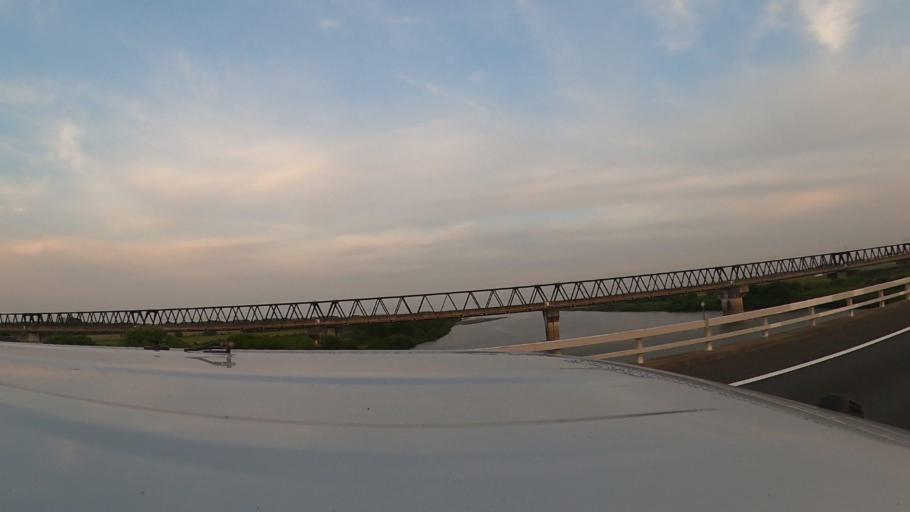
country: JP
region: Ibaraki
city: Moriya
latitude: 35.9296
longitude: 139.9623
